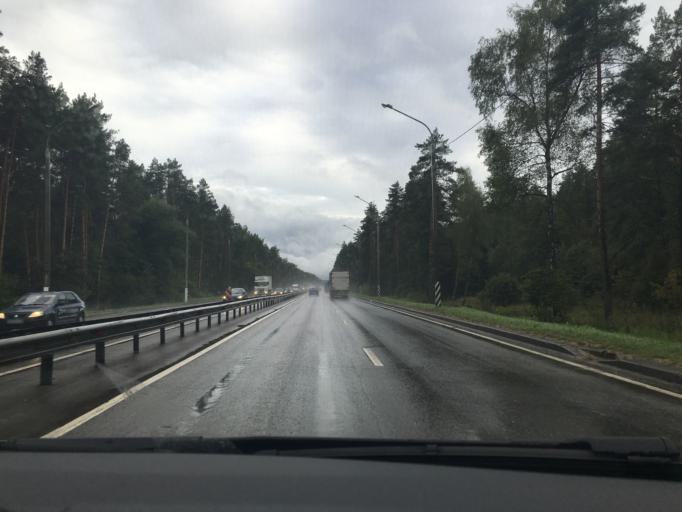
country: RU
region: Kaluga
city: Obninsk
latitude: 55.0650
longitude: 36.6227
